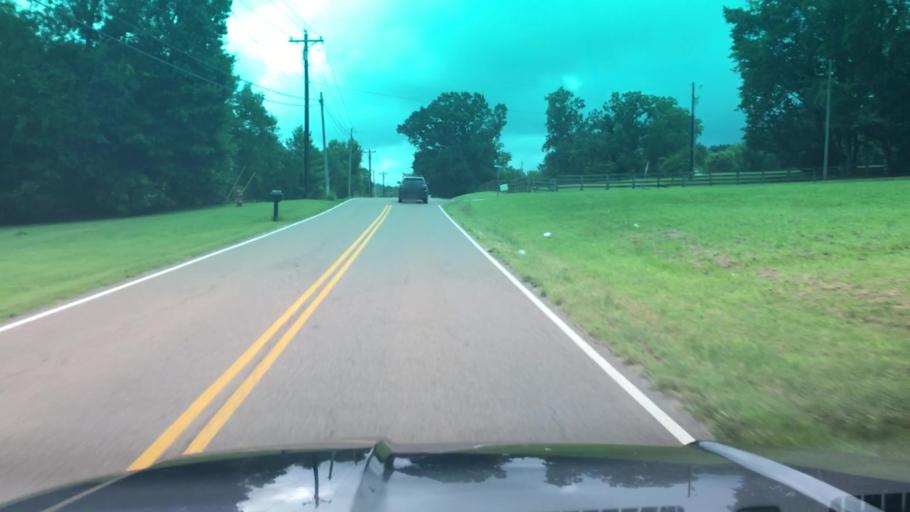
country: US
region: Tennessee
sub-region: Williamson County
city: Thompson's Station
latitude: 35.8079
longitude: -86.8563
